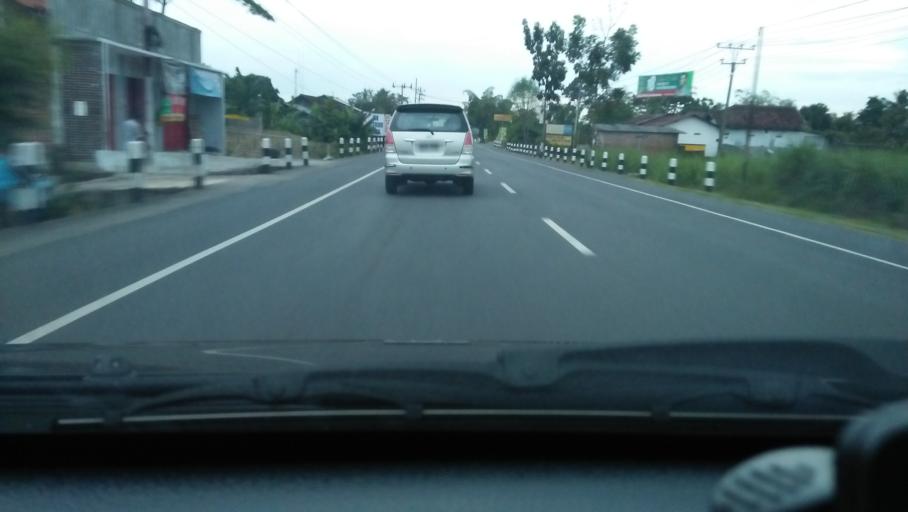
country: ID
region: Central Java
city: Magelang
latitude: -7.4178
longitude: 110.2340
